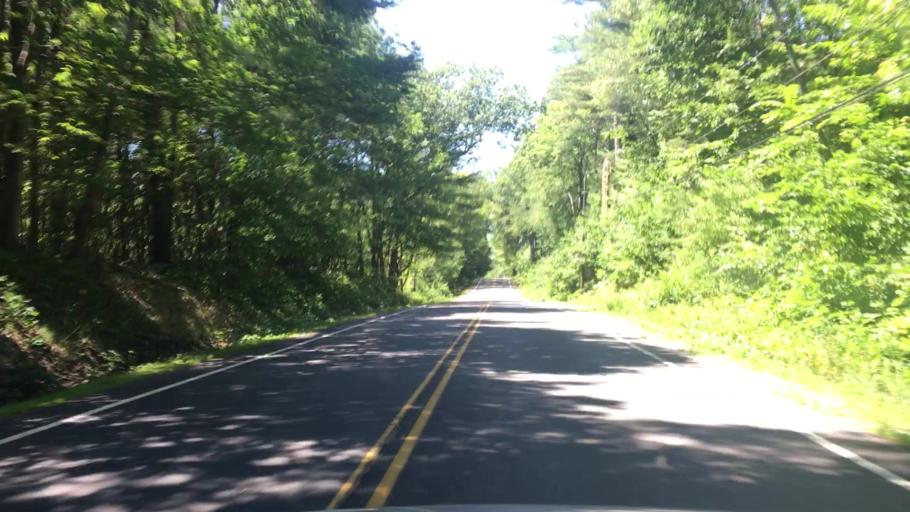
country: US
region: New Hampshire
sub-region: Merrimack County
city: Hopkinton
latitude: 43.1876
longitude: -71.6827
